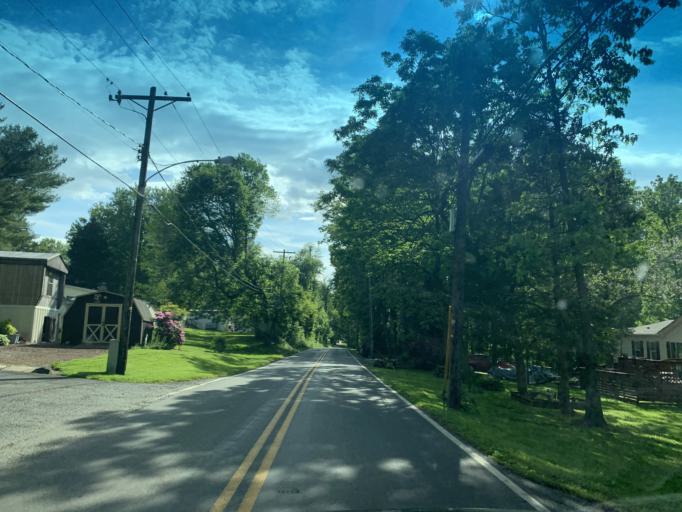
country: US
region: Maryland
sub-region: Cecil County
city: Rising Sun
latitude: 39.6821
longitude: -76.1866
